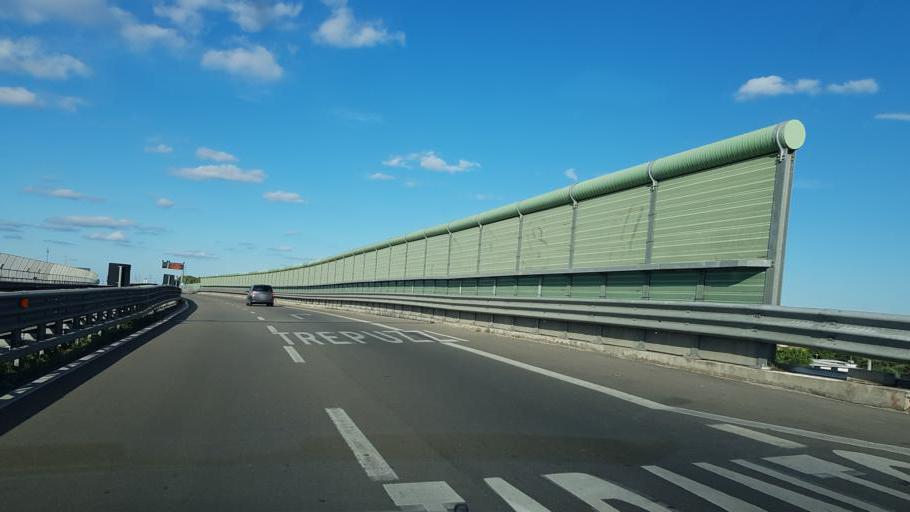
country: IT
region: Apulia
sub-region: Provincia di Lecce
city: Giorgilorio
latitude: 40.3596
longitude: 18.1407
